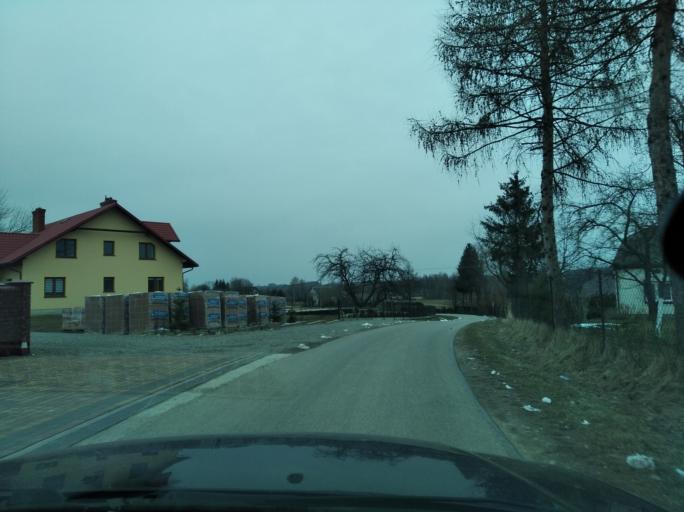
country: PL
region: Subcarpathian Voivodeship
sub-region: Powiat rzeszowski
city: Chmielnik
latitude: 49.9896
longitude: 22.1462
